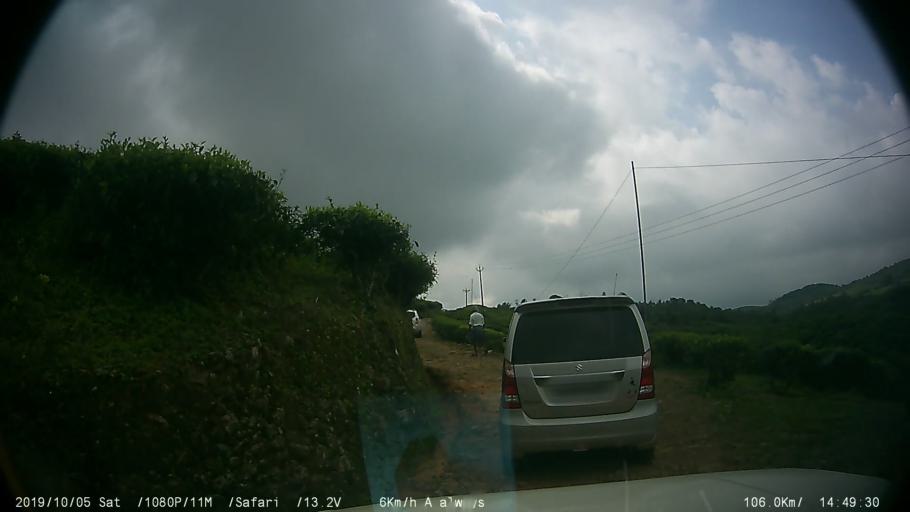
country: IN
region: Kerala
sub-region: Kottayam
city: Erattupetta
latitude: 9.6182
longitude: 76.9392
